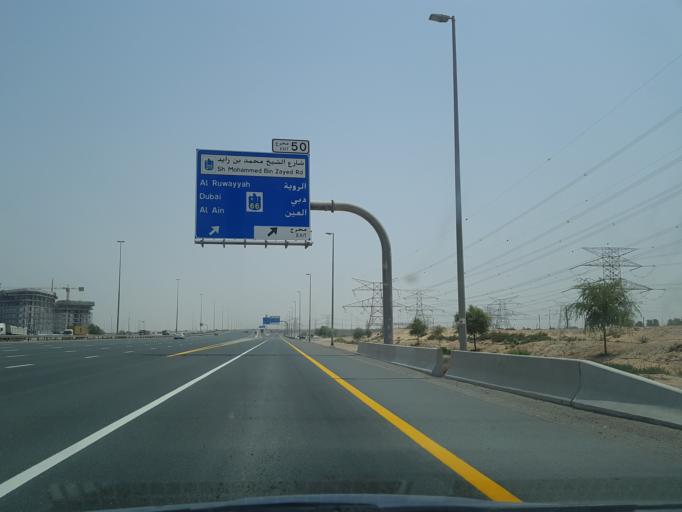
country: AE
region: Dubai
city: Dubai
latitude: 25.0824
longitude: 55.3856
